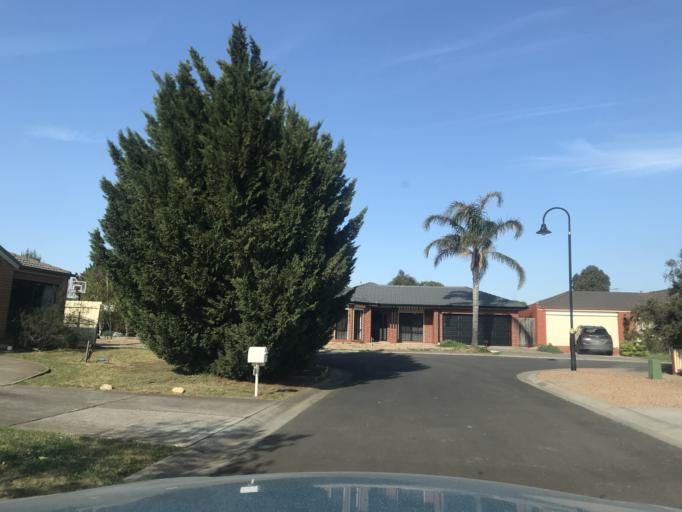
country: AU
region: Victoria
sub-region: Wyndham
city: Williams Landing
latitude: -37.8553
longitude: 144.7175
